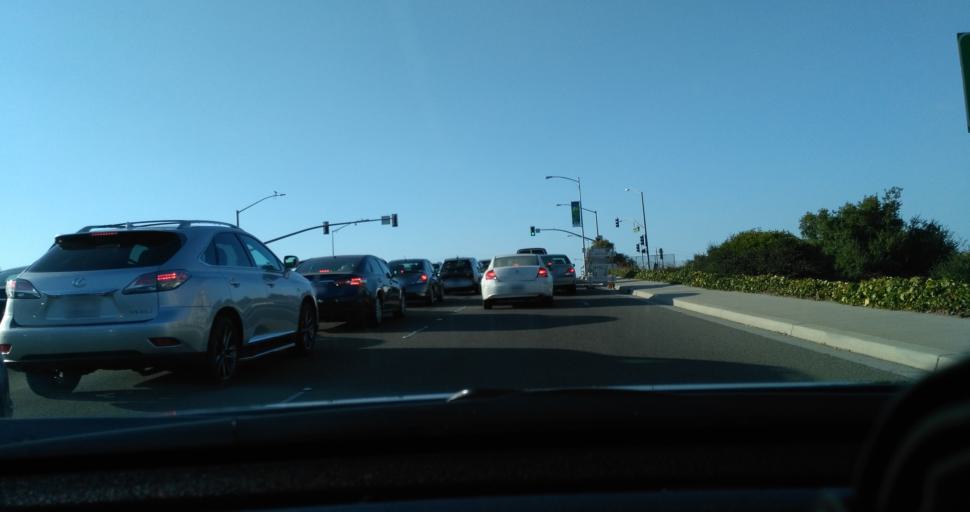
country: US
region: California
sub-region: Santa Clara County
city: Milpitas
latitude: 37.4221
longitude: -121.9225
